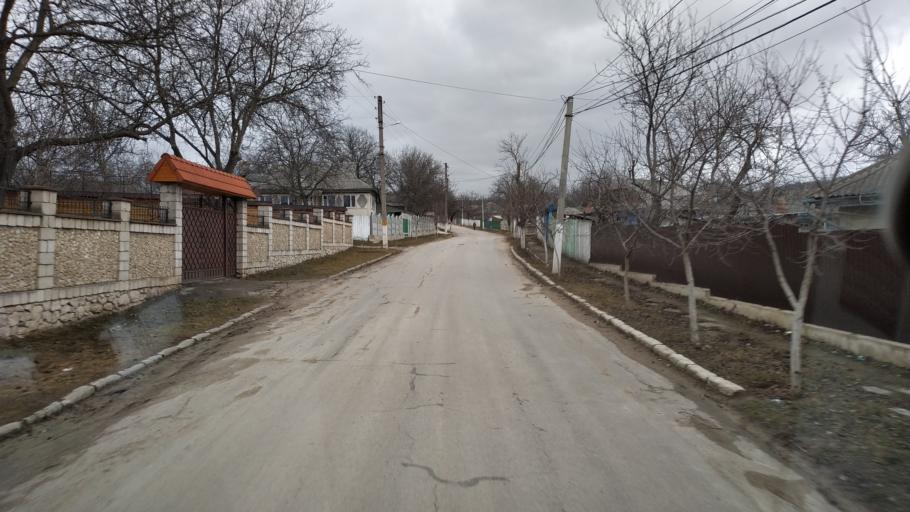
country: MD
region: Calarasi
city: Calarasi
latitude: 47.2603
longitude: 28.1364
